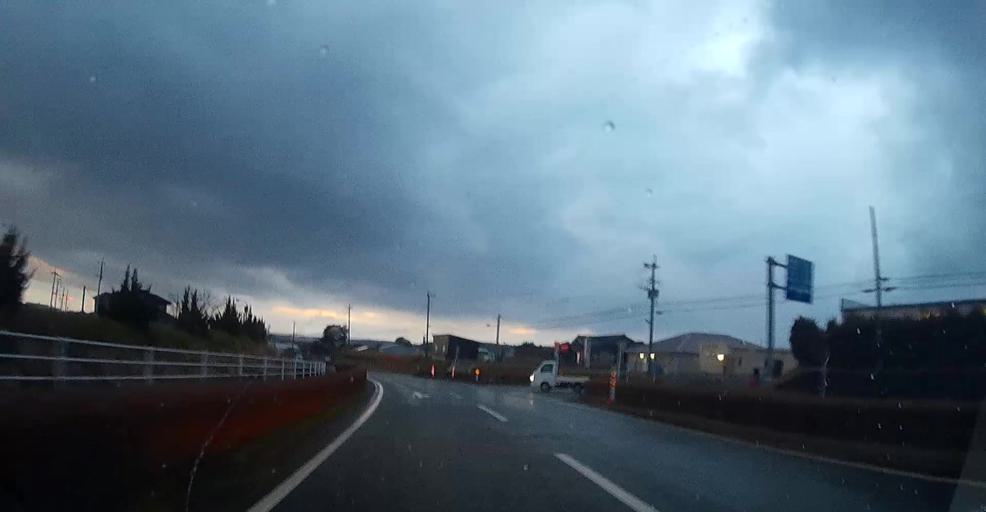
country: JP
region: Kumamoto
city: Ozu
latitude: 32.8393
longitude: 130.9096
